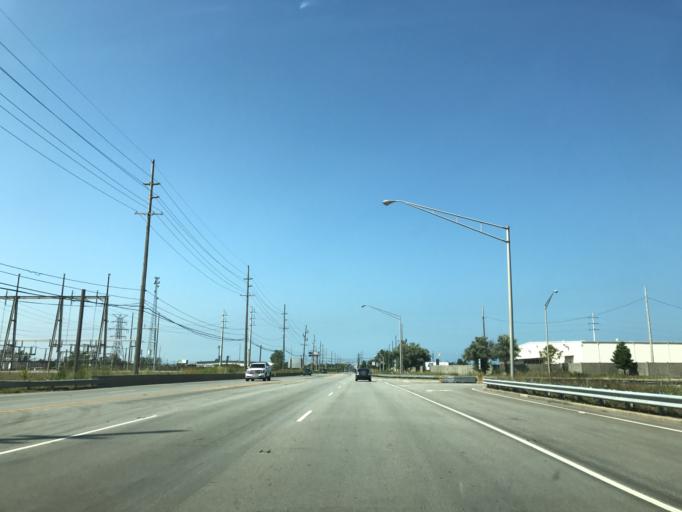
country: US
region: Indiana
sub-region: Lake County
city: Whiting
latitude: 41.6575
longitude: -87.5086
